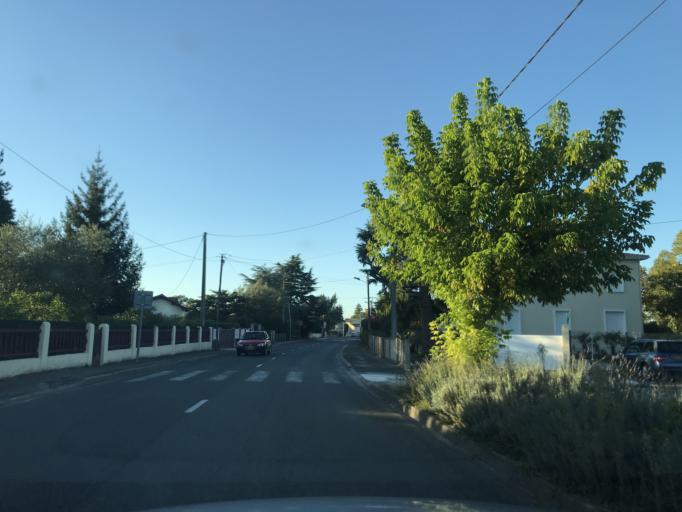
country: FR
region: Aquitaine
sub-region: Departement de la Gironde
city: Saint-Medard-de-Guizieres
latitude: 45.0119
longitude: -0.0544
